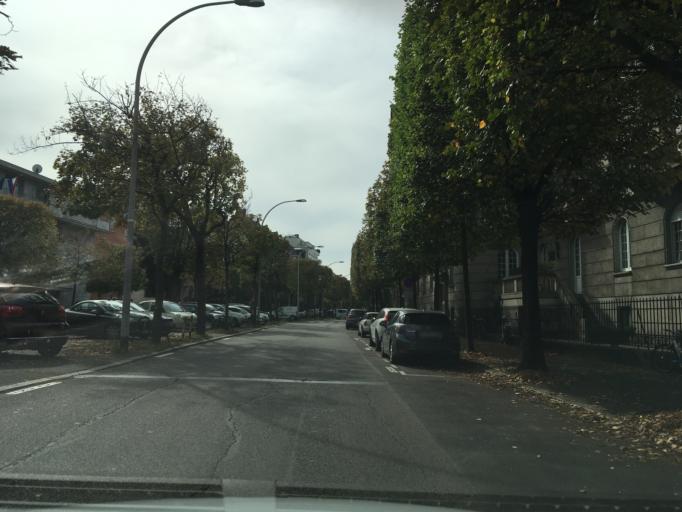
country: FR
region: Alsace
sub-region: Departement du Bas-Rhin
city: Strasbourg
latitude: 48.5917
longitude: 7.7693
